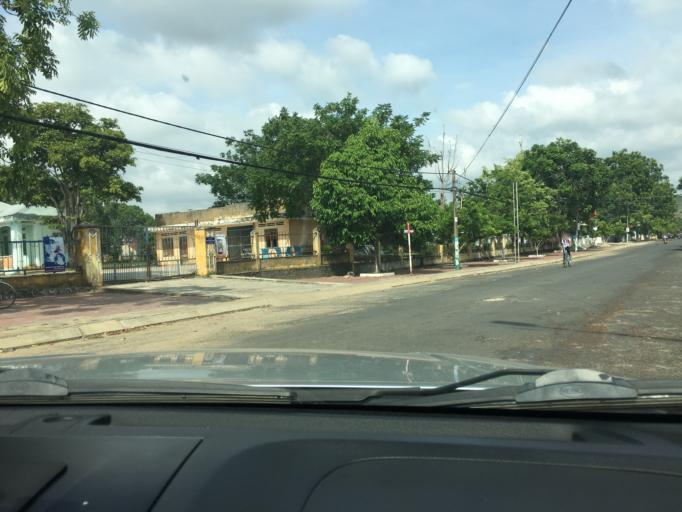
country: VN
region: Gia Lai
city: Kong Chro
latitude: 13.7750
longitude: 108.5243
